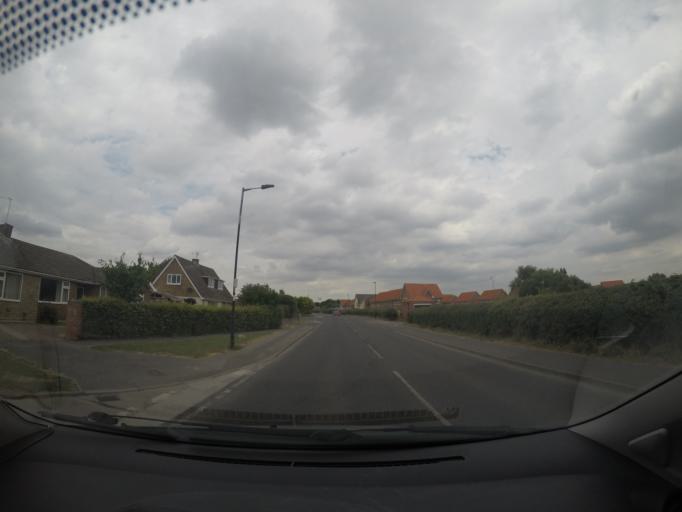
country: GB
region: England
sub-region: City of York
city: Huntington
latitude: 53.9900
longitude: -1.0591
